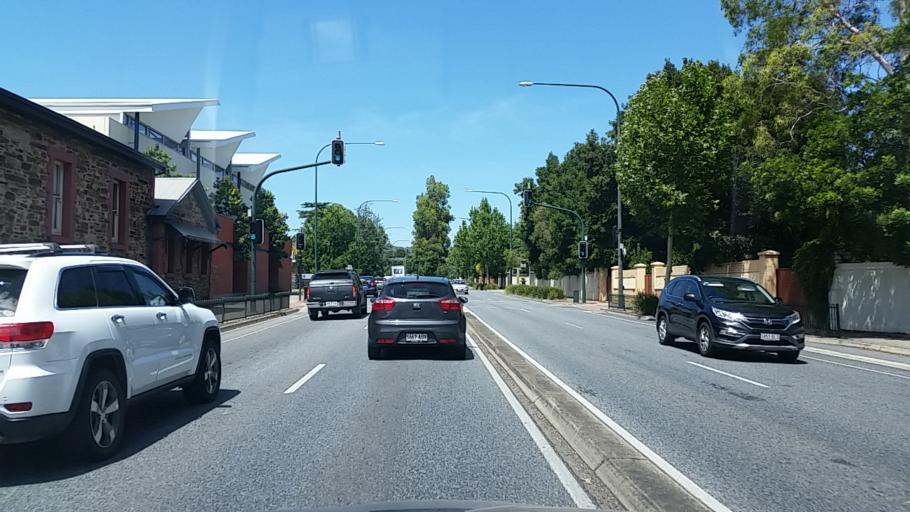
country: AU
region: South Australia
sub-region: Norwood Payneham St Peters
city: Trinity Gardens
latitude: -34.9282
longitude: 138.6416
